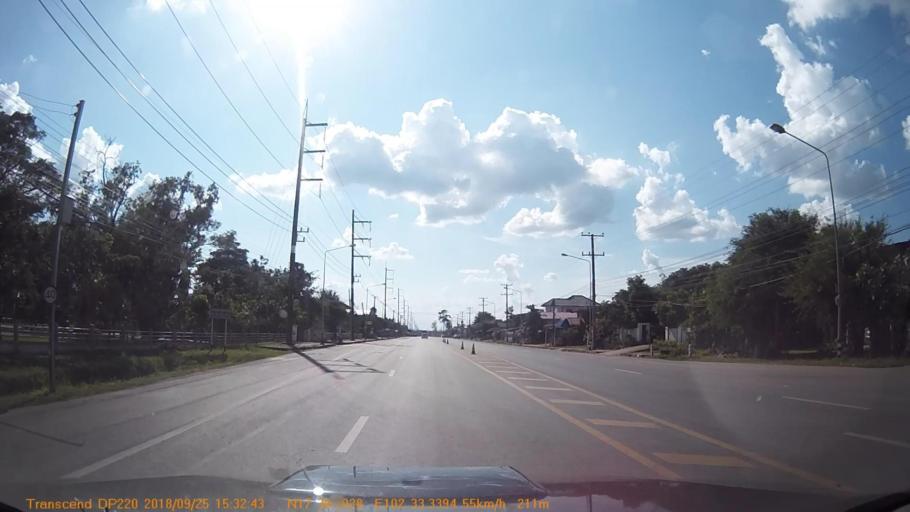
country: TH
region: Changwat Udon Thani
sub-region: Amphoe Ban Phue
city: Ban Phue
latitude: 17.6034
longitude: 102.5558
